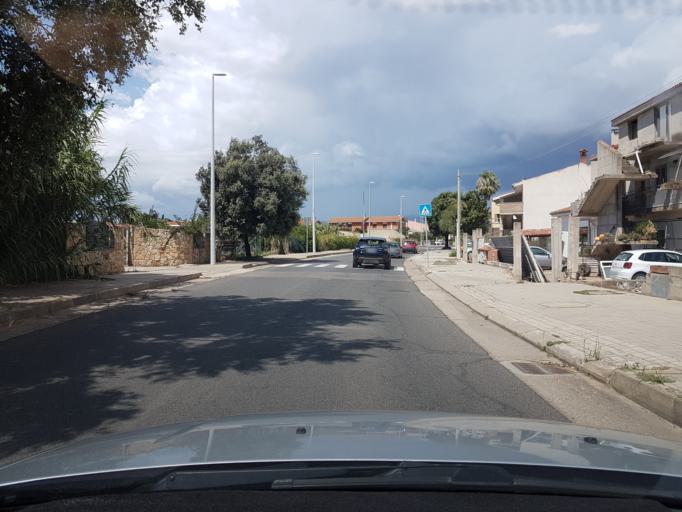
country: IT
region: Sardinia
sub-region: Provincia di Oristano
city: Riola Sardo
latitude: 39.9882
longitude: 8.5408
